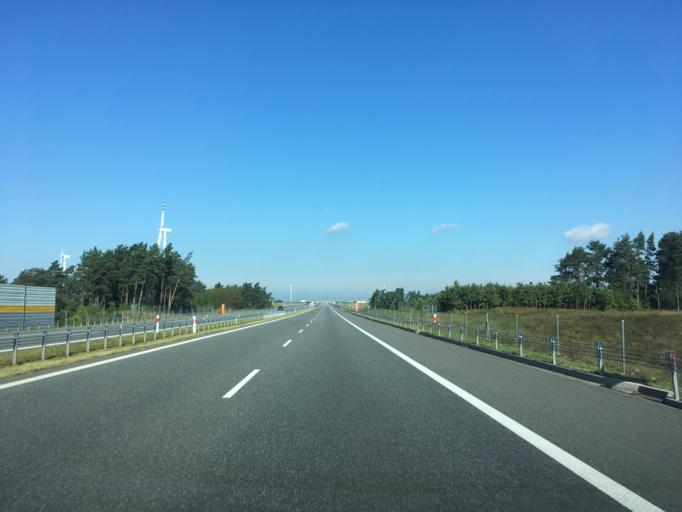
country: PL
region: Kujawsko-Pomorskie
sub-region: Powiat chelminski
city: Lisewo
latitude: 53.3571
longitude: 18.7026
